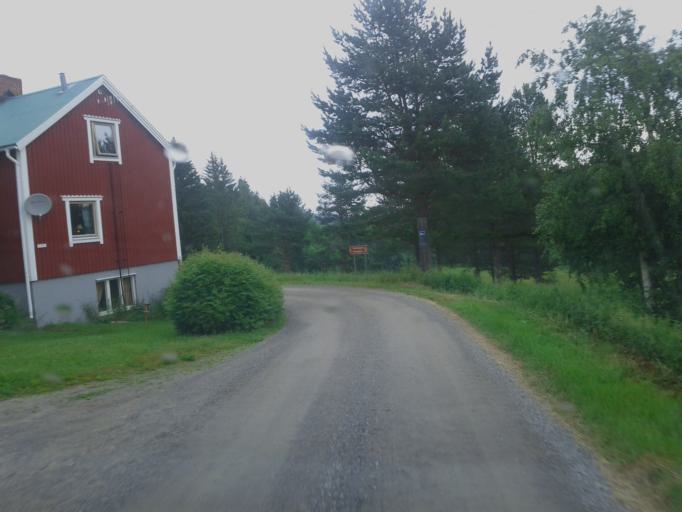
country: SE
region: Vaesternorrland
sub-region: OErnskoeldsviks Kommun
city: Bjasta
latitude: 63.0727
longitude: 18.4452
